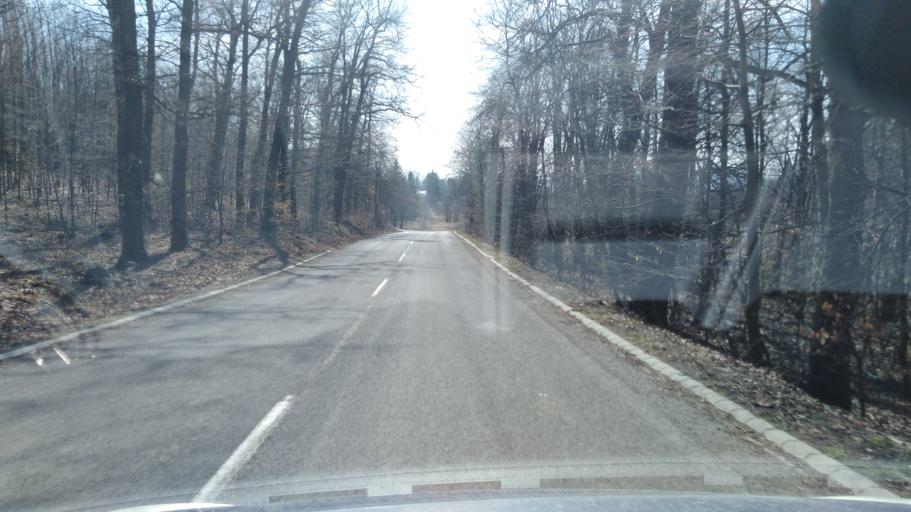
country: HU
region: Nograd
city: Somoskoujfalu
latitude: 48.1487
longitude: 19.8618
